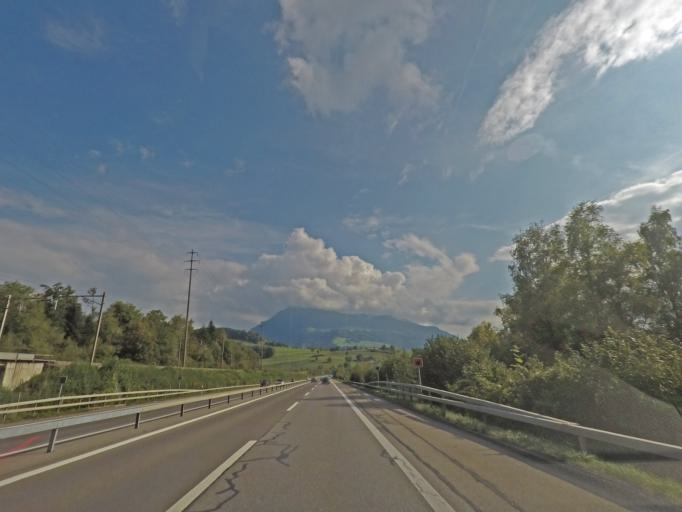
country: CH
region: Lucerne
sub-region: Lucerne-Land District
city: Meierskappel
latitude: 47.1186
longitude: 8.4528
